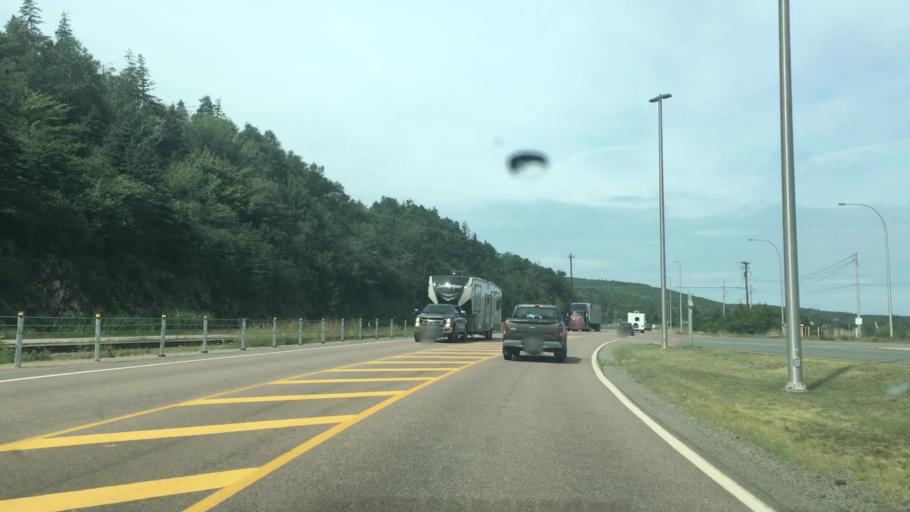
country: CA
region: Nova Scotia
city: Port Hawkesbury
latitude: 45.6419
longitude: -61.4292
